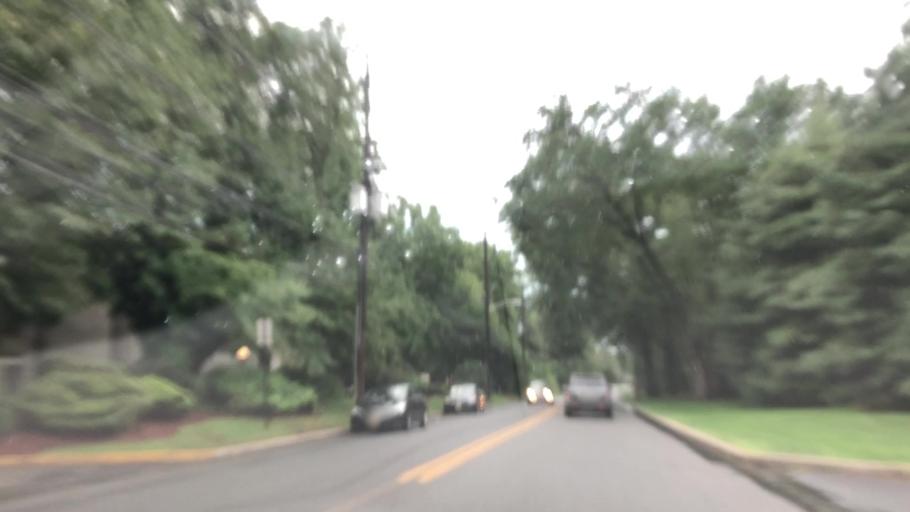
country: US
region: New Jersey
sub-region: Bergen County
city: Lyndhurst
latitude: 40.8205
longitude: -74.1359
